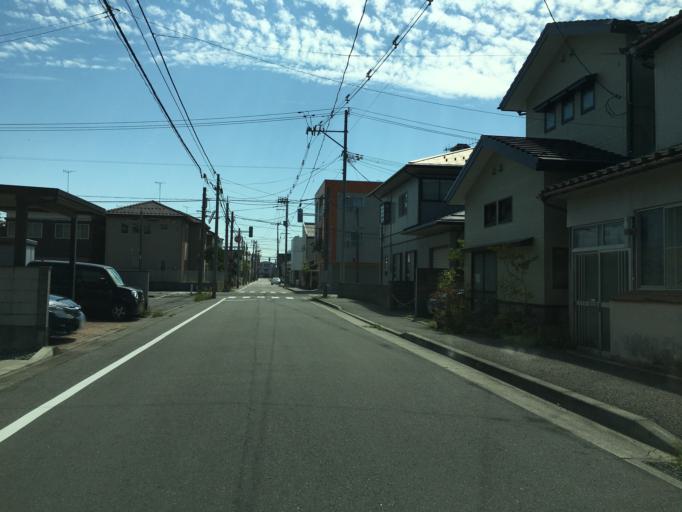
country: JP
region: Niigata
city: Niigata-shi
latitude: 37.9128
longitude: 139.0232
